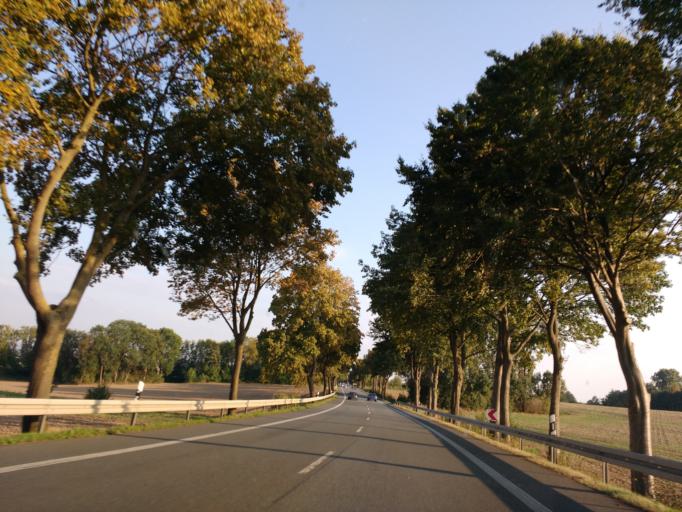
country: DE
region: North Rhine-Westphalia
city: Warburg
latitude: 51.5654
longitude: 9.1299
